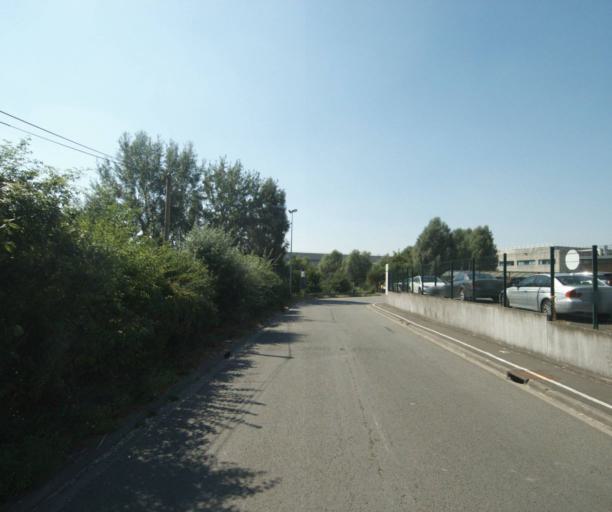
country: FR
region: Nord-Pas-de-Calais
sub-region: Departement du Nord
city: Bousbecque
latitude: 50.7702
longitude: 3.0898
